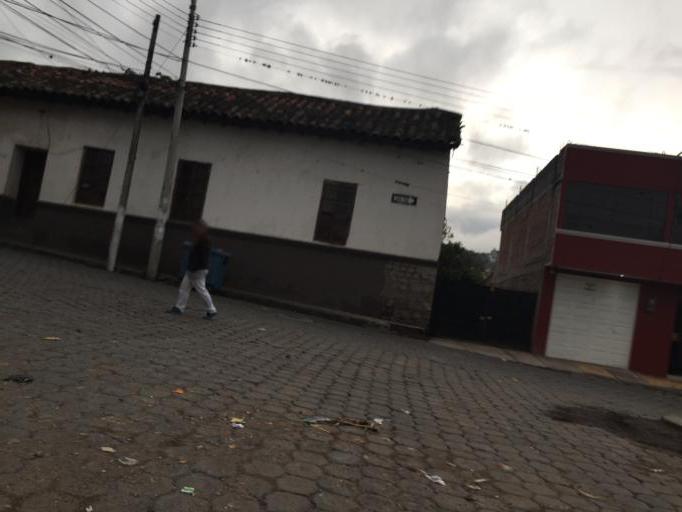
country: EC
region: Imbabura
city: Atuntaqui
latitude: 0.3347
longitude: -78.1707
